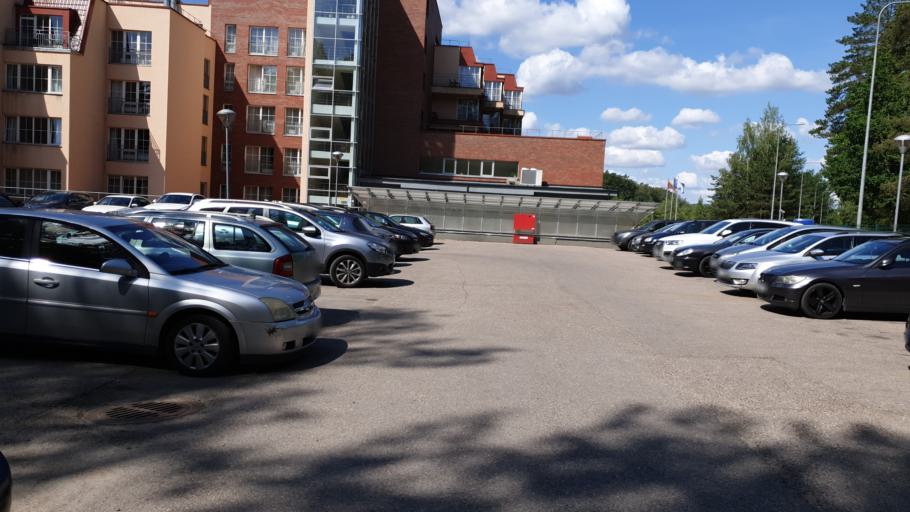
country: LT
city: Birstonas
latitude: 54.6051
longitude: 23.9976
